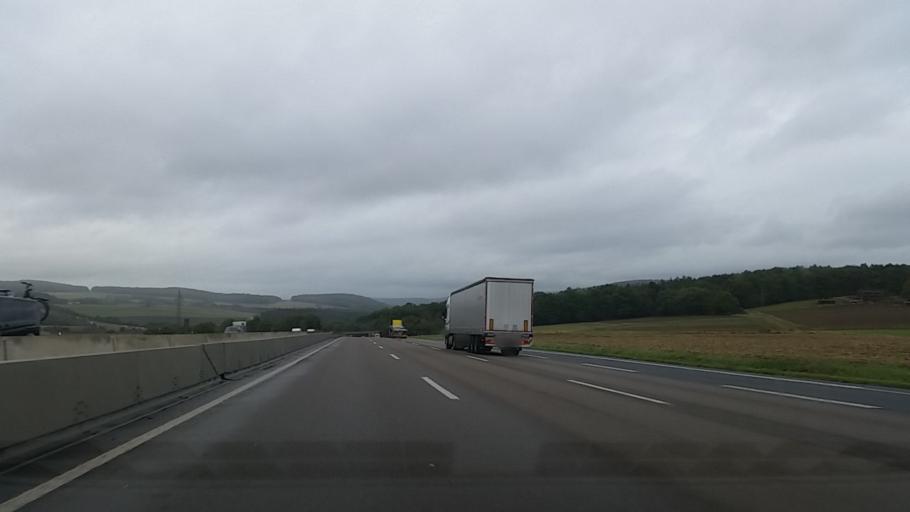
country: DE
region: Hesse
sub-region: Regierungsbezirk Kassel
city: Malsfeld
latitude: 51.0391
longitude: 9.4915
